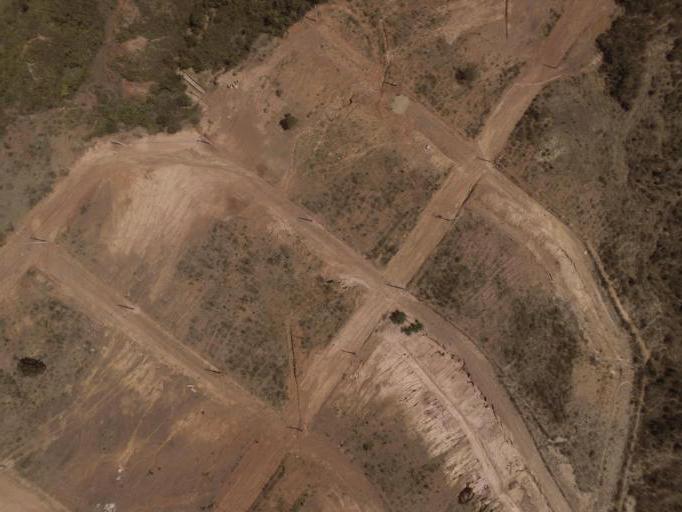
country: BR
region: Minas Gerais
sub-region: Tiradentes
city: Tiradentes
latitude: -21.0501
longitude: -44.0858
